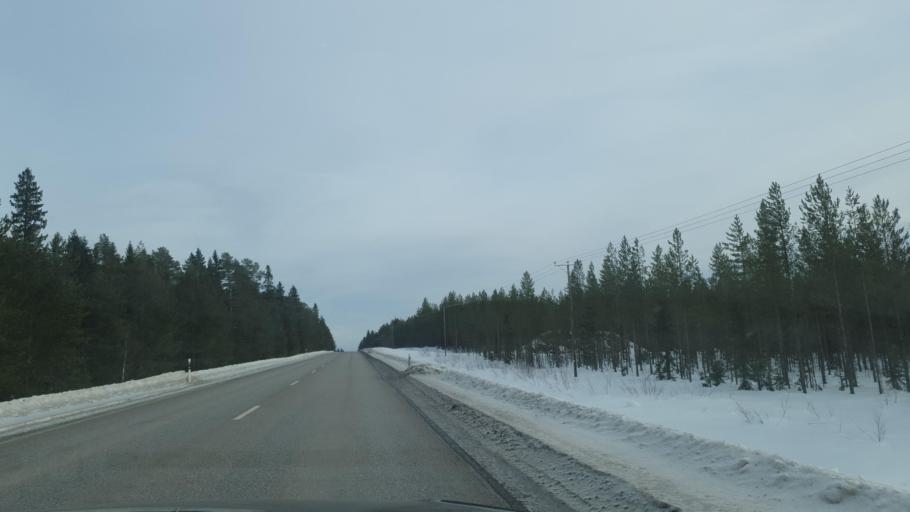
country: FI
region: Kainuu
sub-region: Kajaani
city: Vaala
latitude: 64.5355
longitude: 27.2191
